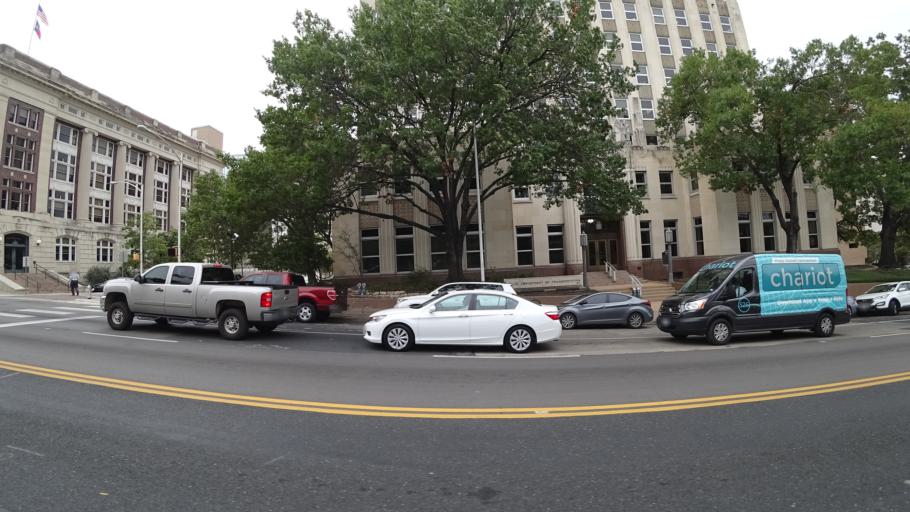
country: US
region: Texas
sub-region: Travis County
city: Austin
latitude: 30.2724
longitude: -97.7400
